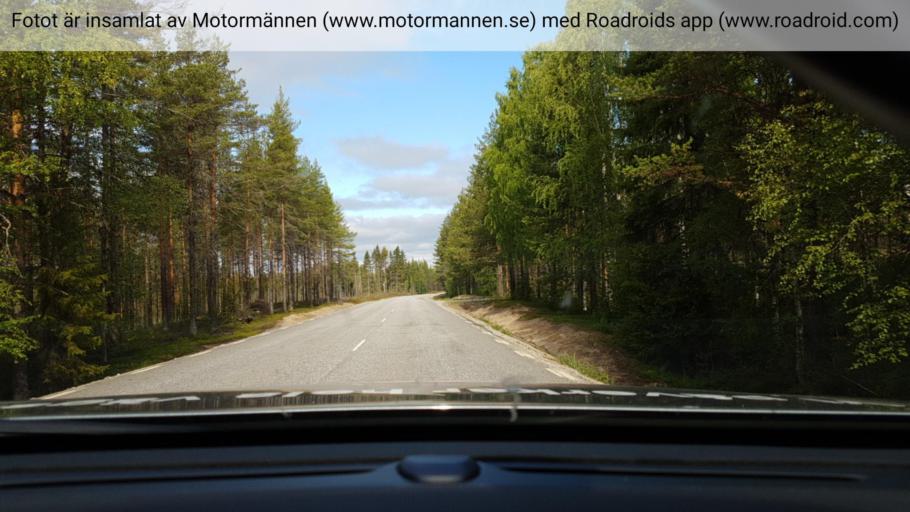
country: SE
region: Vaesterbotten
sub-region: Norsjo Kommun
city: Norsjoe
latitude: 64.6964
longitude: 19.1801
